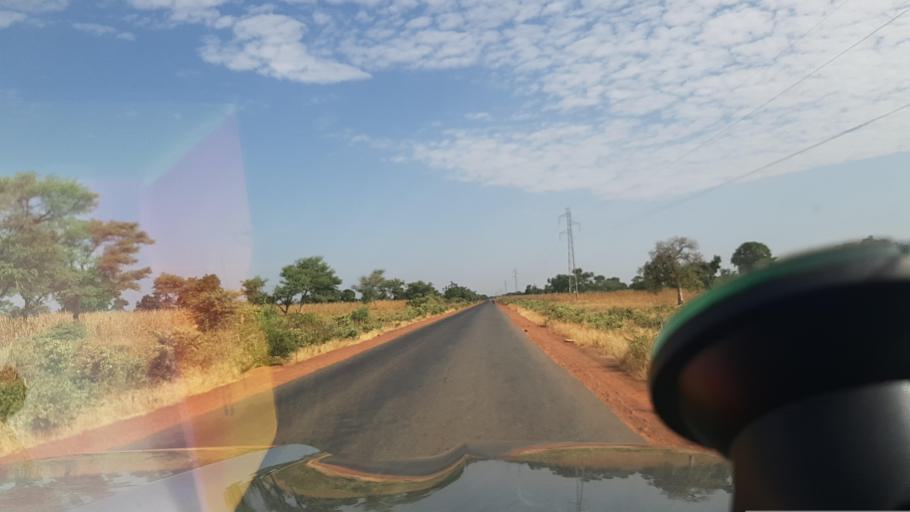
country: ML
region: Segou
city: Markala
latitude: 13.5556
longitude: -6.1144
